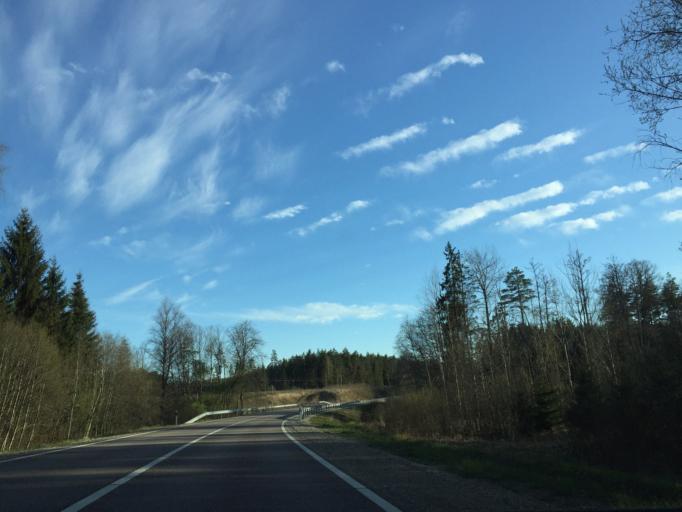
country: LV
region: Valkas Rajons
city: Valka
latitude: 57.7169
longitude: 25.9330
